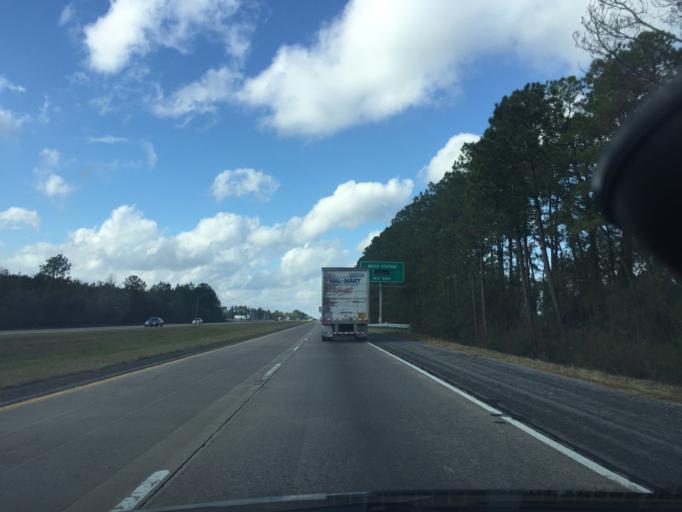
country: US
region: Georgia
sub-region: Chatham County
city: Bloomingdale
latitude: 32.1643
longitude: -81.4376
